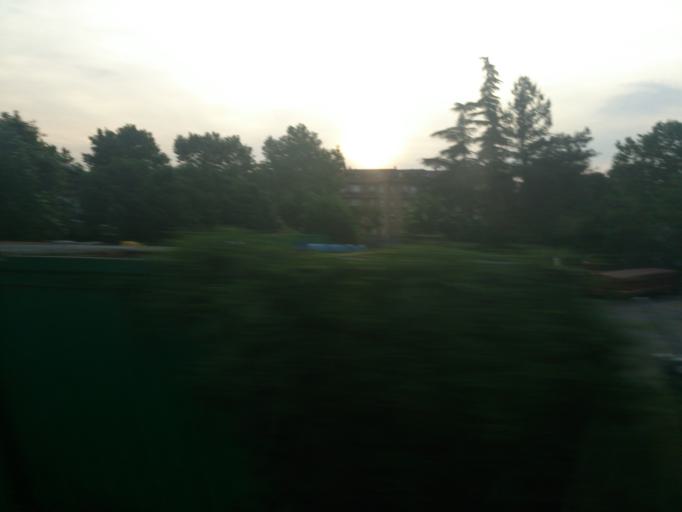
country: IT
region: Lombardy
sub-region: Provincia di Bergamo
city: Azzano San Paolo
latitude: 45.6704
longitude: 9.6672
